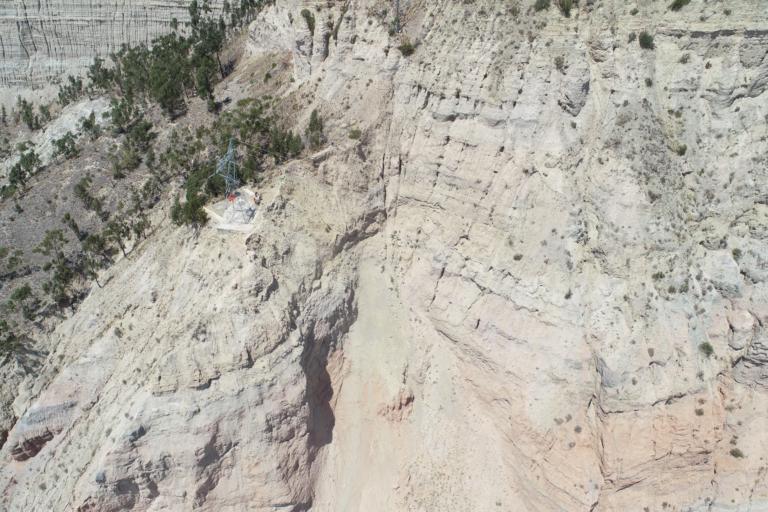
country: BO
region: La Paz
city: La Paz
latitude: -16.5287
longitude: -68.0899
